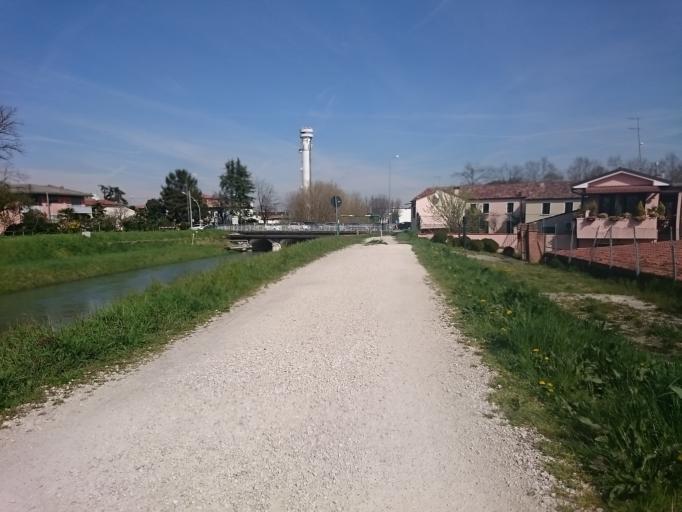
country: IT
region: Veneto
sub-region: Provincia di Padova
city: Caselle
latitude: 45.4165
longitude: 11.8276
